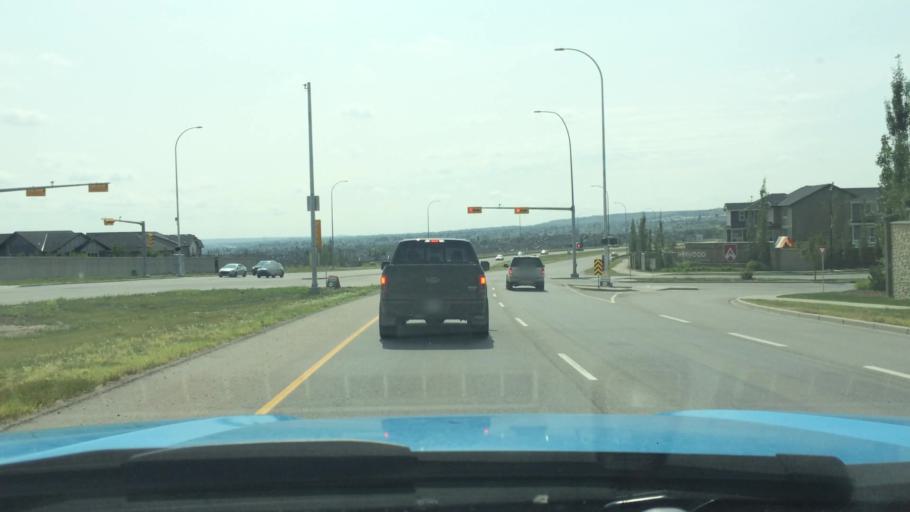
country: CA
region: Alberta
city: Calgary
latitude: 51.1638
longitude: -114.1445
